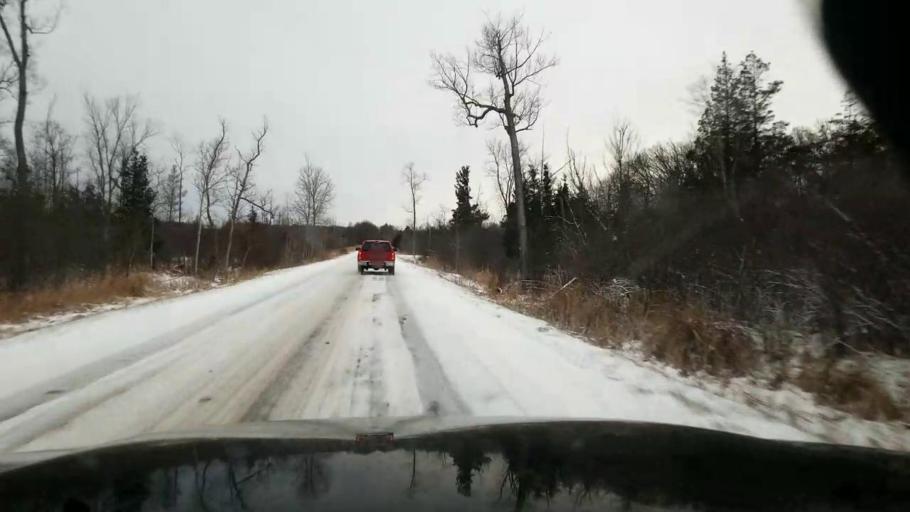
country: US
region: Michigan
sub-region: Jackson County
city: Spring Arbor
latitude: 42.1284
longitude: -84.4984
